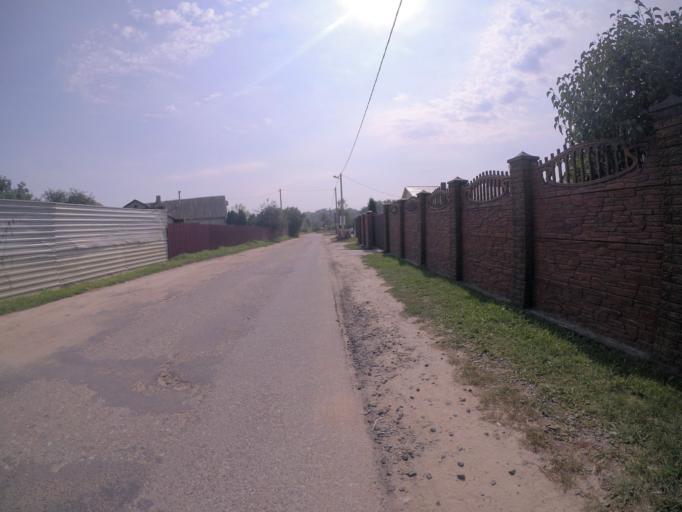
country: BY
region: Grodnenskaya
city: Hrodna
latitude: 53.7204
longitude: 23.8469
